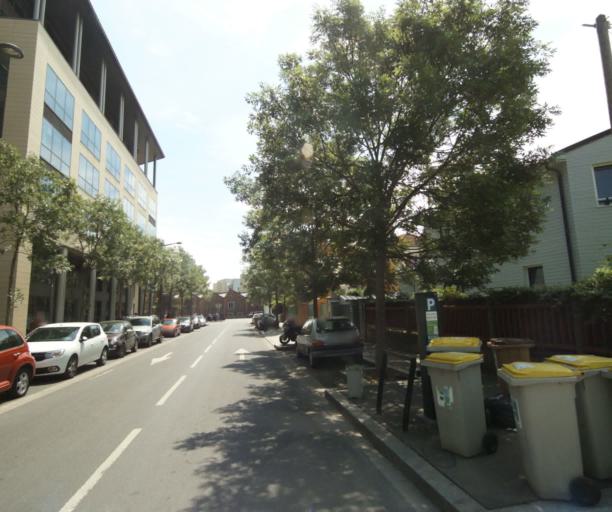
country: FR
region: Ile-de-France
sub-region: Departement des Hauts-de-Seine
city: Courbevoie
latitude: 48.9069
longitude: 2.2580
